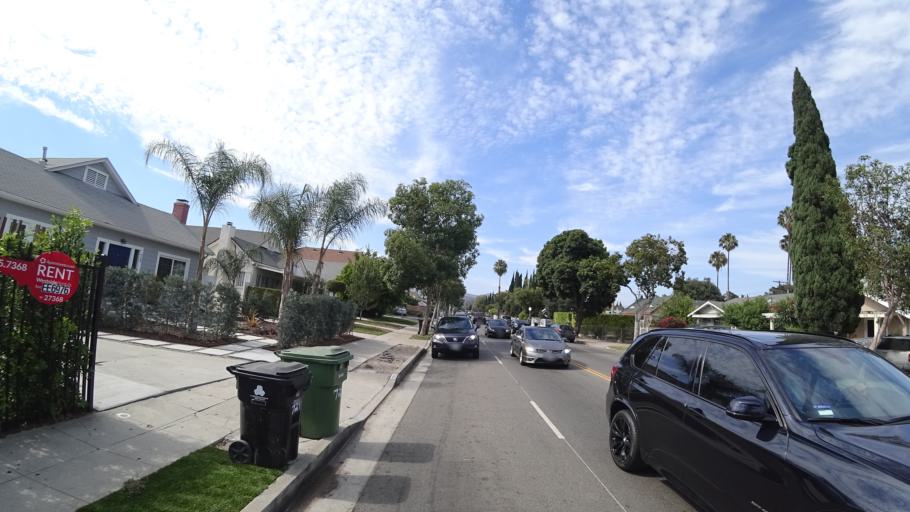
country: US
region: California
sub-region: Los Angeles County
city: Hollywood
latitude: 34.0844
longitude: -118.3136
